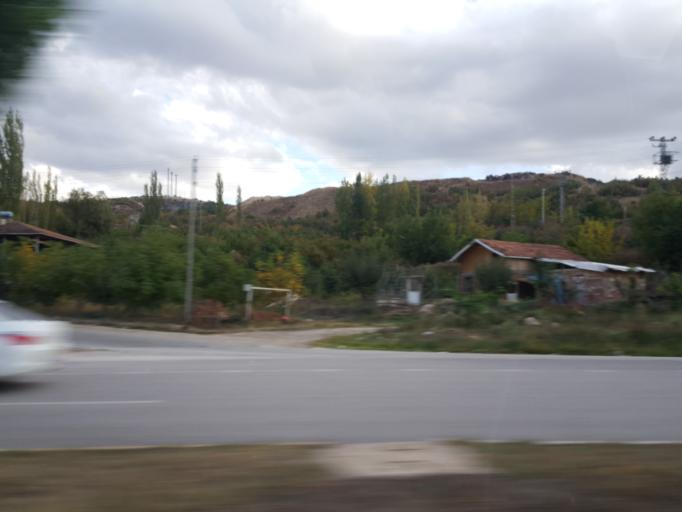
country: TR
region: Tokat
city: Tokat
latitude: 40.3358
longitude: 36.4875
